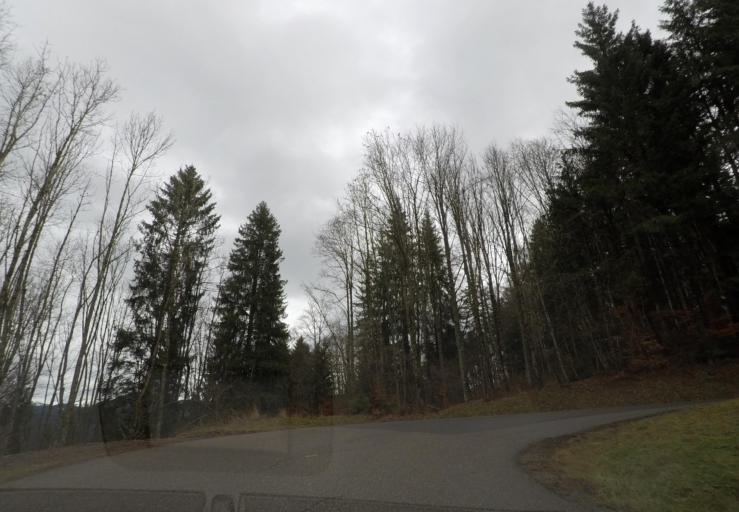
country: FR
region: Rhone-Alpes
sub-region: Departement de la Haute-Savoie
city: Chatillon-sur-Cluses
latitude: 46.0817
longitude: 6.6125
